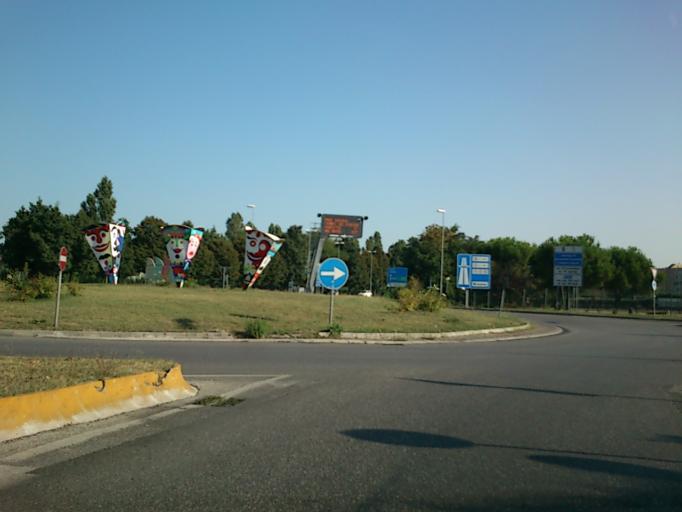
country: IT
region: The Marches
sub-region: Provincia di Pesaro e Urbino
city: Fano
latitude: 43.8319
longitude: 13.0132
